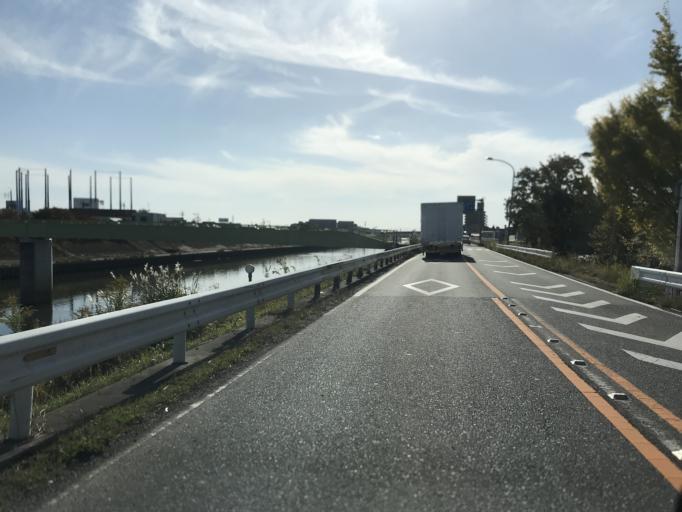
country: JP
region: Aichi
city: Nagoya-shi
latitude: 35.2102
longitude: 136.8615
